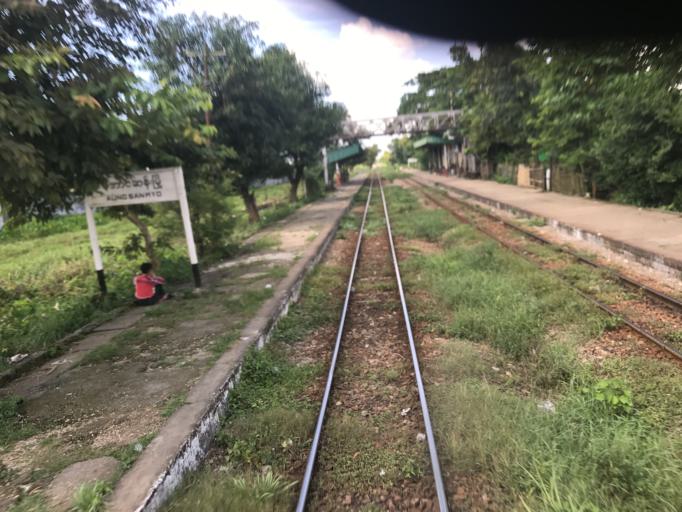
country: MM
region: Yangon
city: Yangon
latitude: 16.9143
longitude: 96.0929
